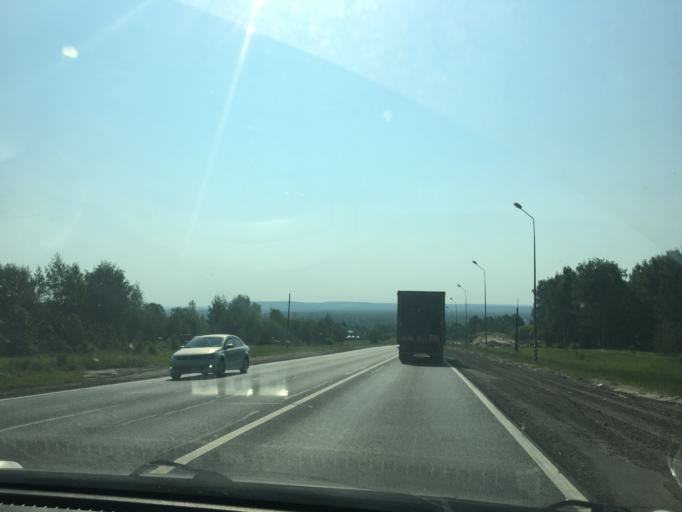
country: RU
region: Nizjnij Novgorod
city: Kstovo
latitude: 56.1044
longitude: 44.2934
